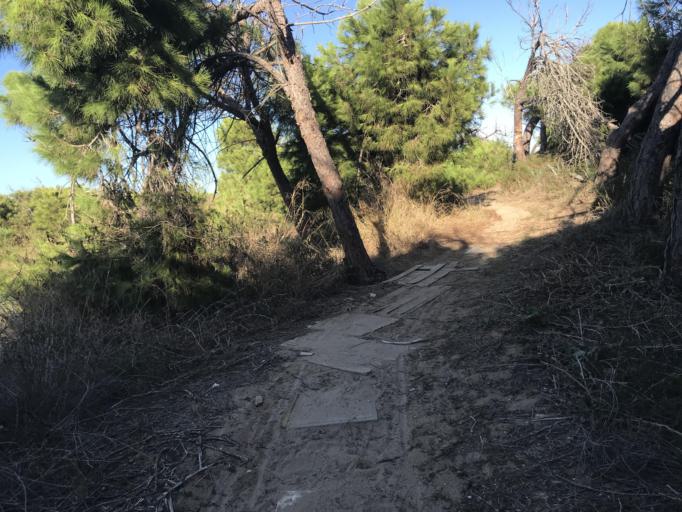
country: ES
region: Valencia
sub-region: Provincia de Alicante
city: Guardamar del Segura
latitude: 38.0315
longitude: -0.6541
